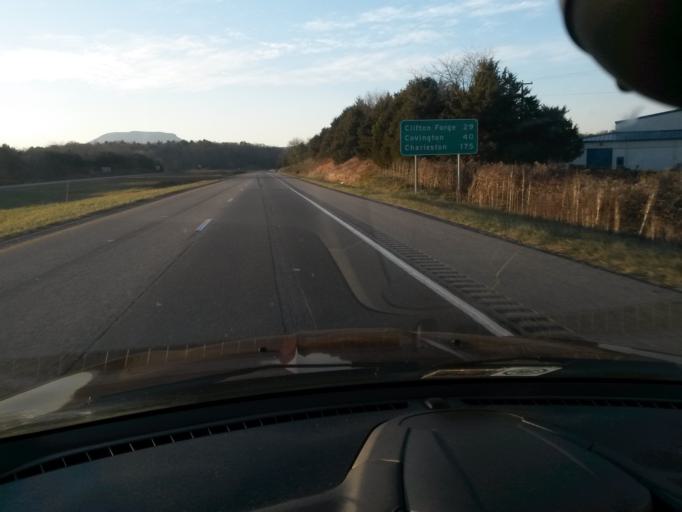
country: US
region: Virginia
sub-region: Rockbridge County
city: East Lexington
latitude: 37.8064
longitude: -79.4267
